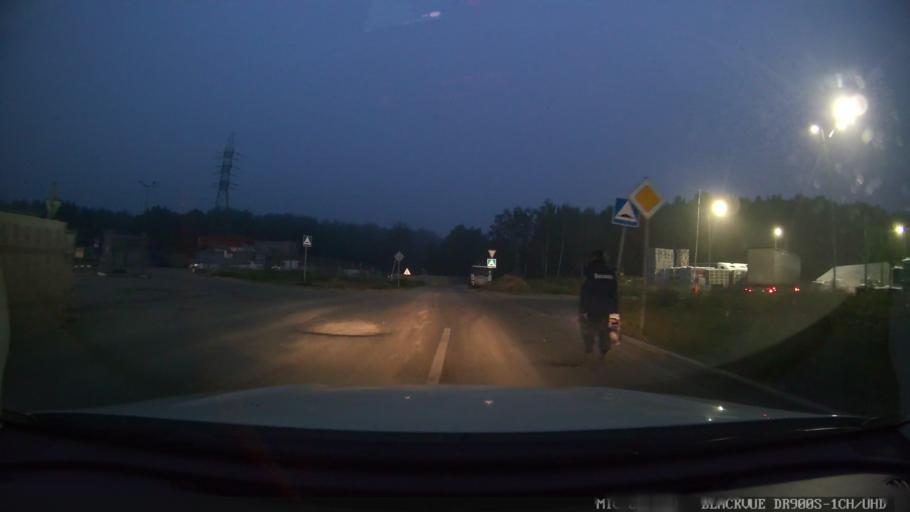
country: RU
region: Moscow
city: Solntsevo
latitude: 55.6208
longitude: 37.3877
